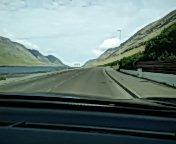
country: FO
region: Nordoyar
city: Klaksvik
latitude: 62.3008
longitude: -6.5223
